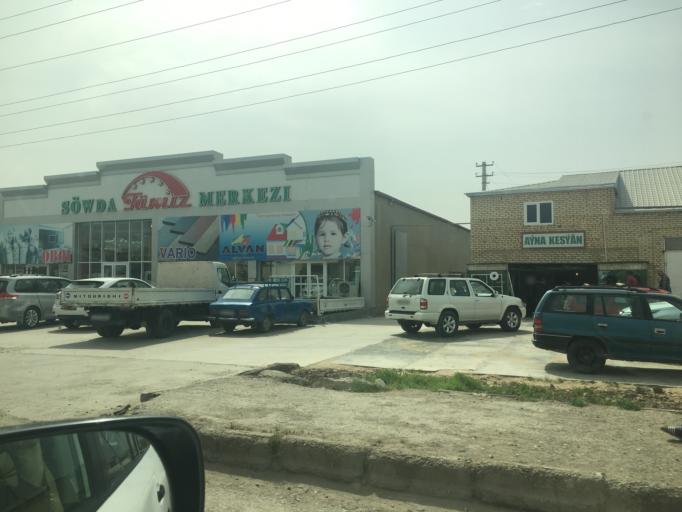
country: TM
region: Mary
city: Mary
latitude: 37.5986
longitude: 61.8549
